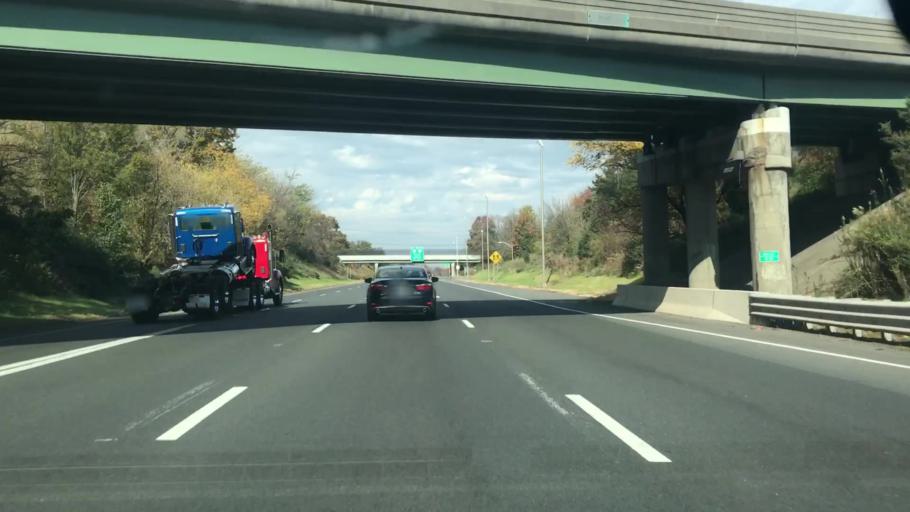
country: US
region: New Jersey
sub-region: Somerset County
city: Bedminster
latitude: 40.6442
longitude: -74.6453
